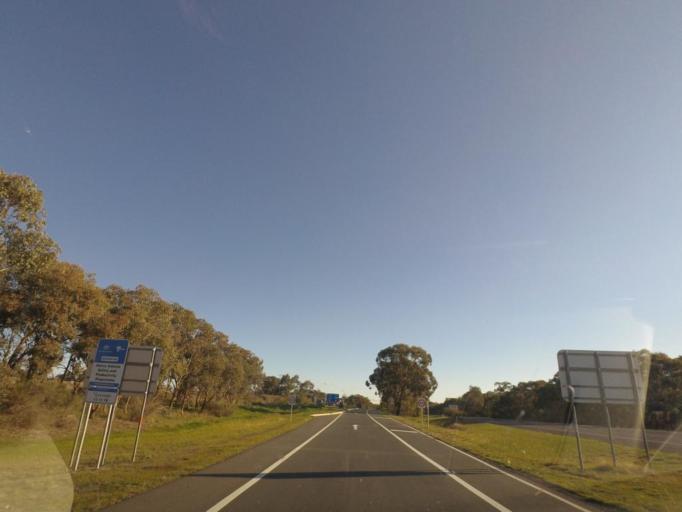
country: AU
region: Victoria
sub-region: Greater Shepparton
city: Shepparton
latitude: -36.7801
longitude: 145.5027
